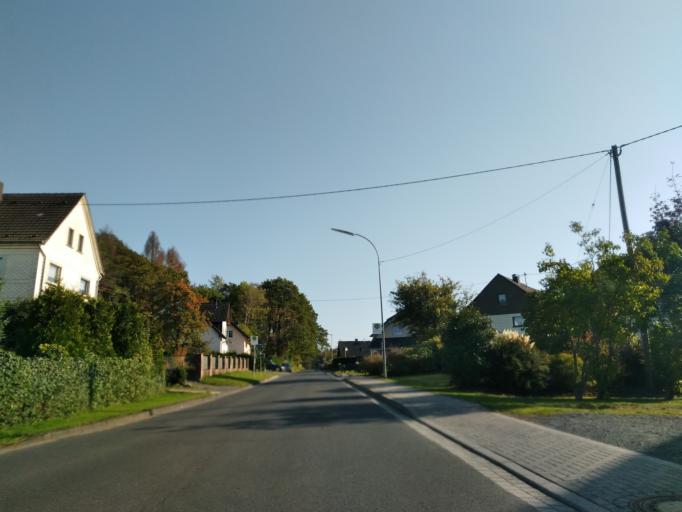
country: DE
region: Rheinland-Pfalz
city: Kircheib
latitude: 50.7087
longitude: 7.4677
